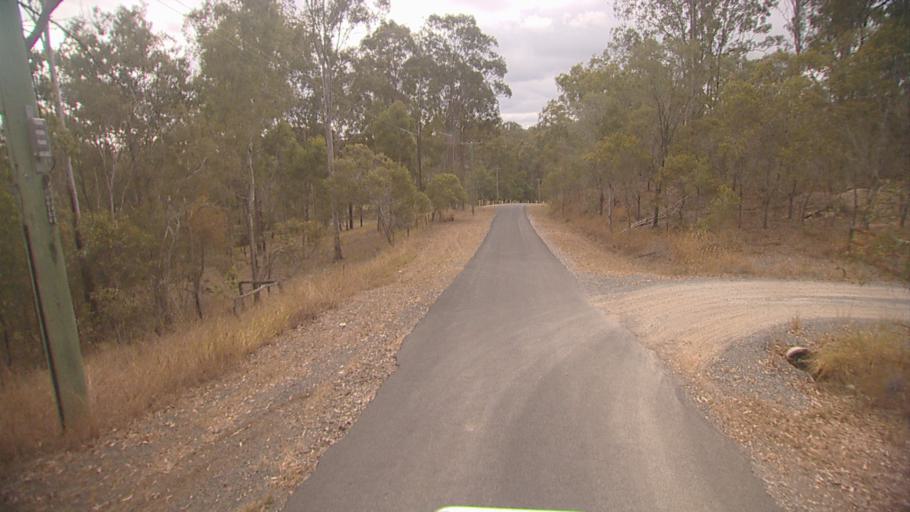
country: AU
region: Queensland
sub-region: Logan
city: Cedar Vale
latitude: -27.8571
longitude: 153.0649
